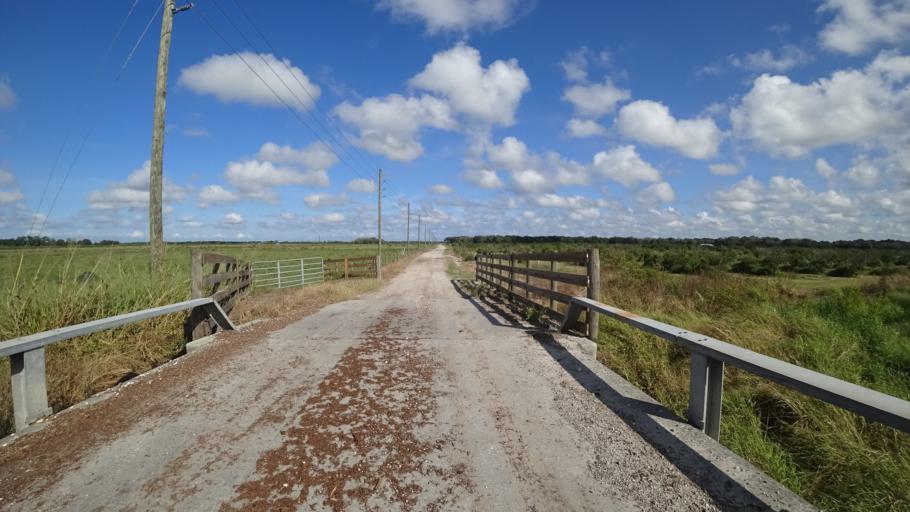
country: US
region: Florida
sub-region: Manatee County
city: Ellenton
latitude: 27.5889
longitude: -82.4746
